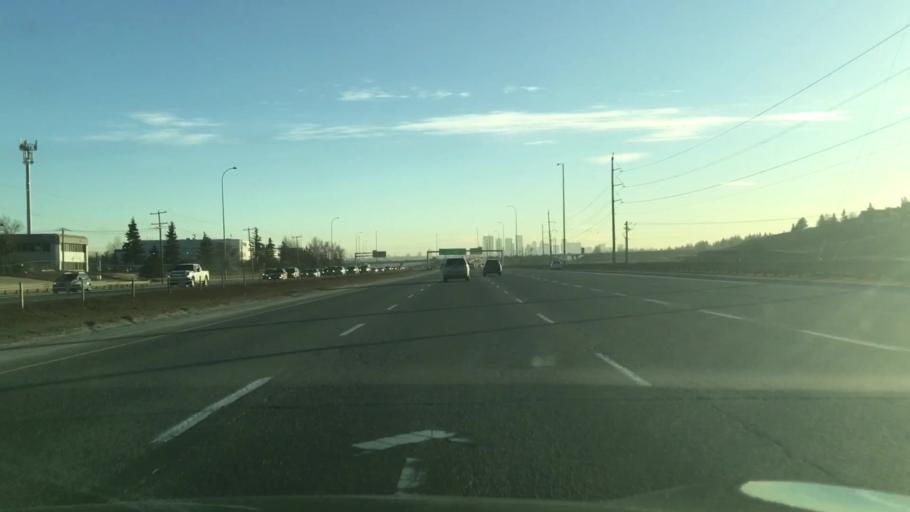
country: CA
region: Alberta
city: Calgary
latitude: 51.1190
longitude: -114.0469
